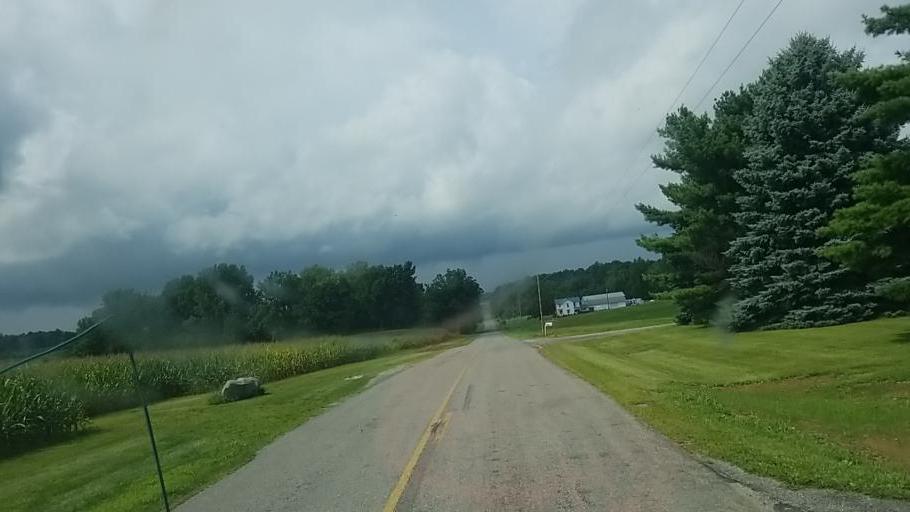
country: US
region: Ohio
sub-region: Champaign County
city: North Lewisburg
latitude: 40.2426
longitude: -83.6475
